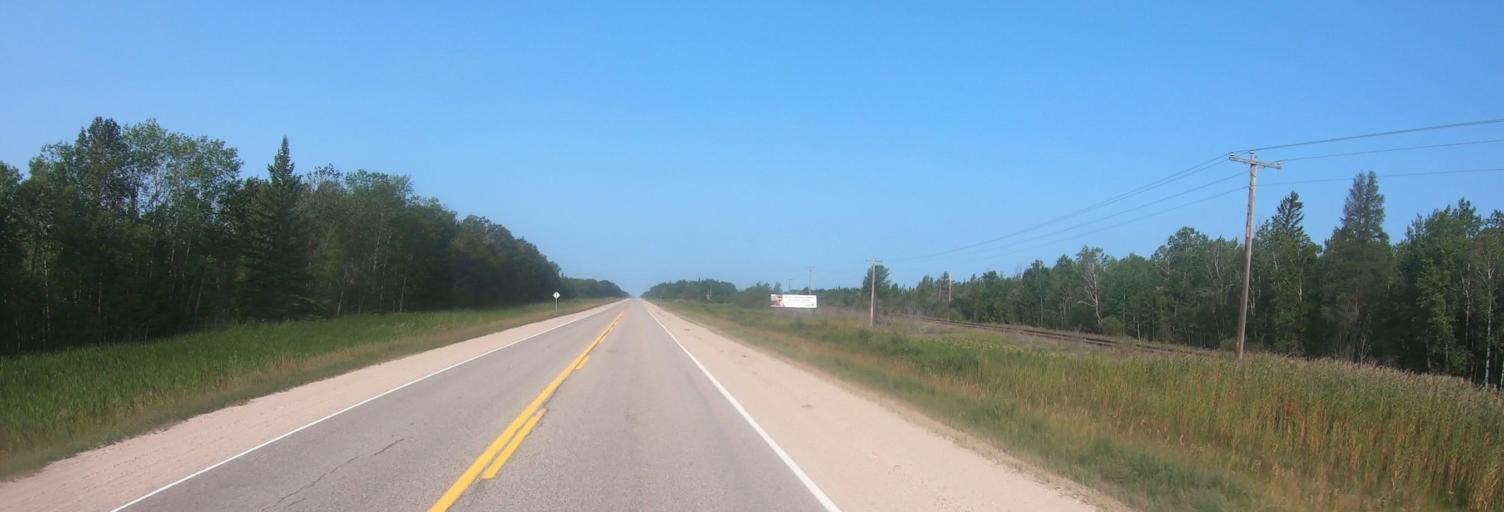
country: US
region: Minnesota
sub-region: Roseau County
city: Warroad
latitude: 49.0162
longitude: -95.4131
